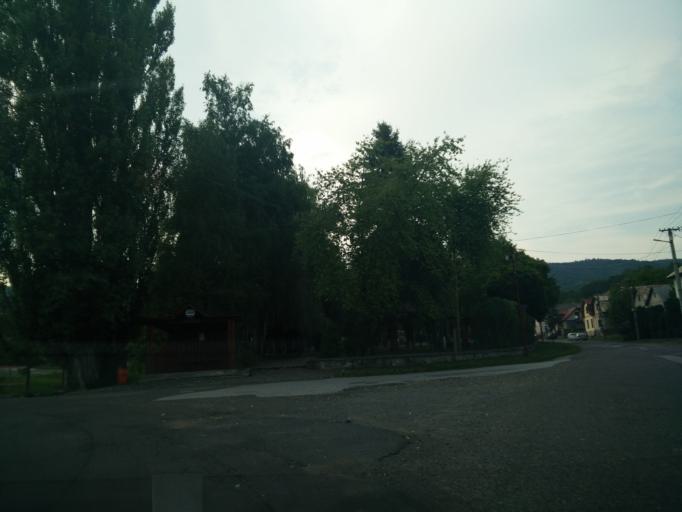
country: SK
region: Nitriansky
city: Handlova
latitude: 48.6554
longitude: 18.7840
